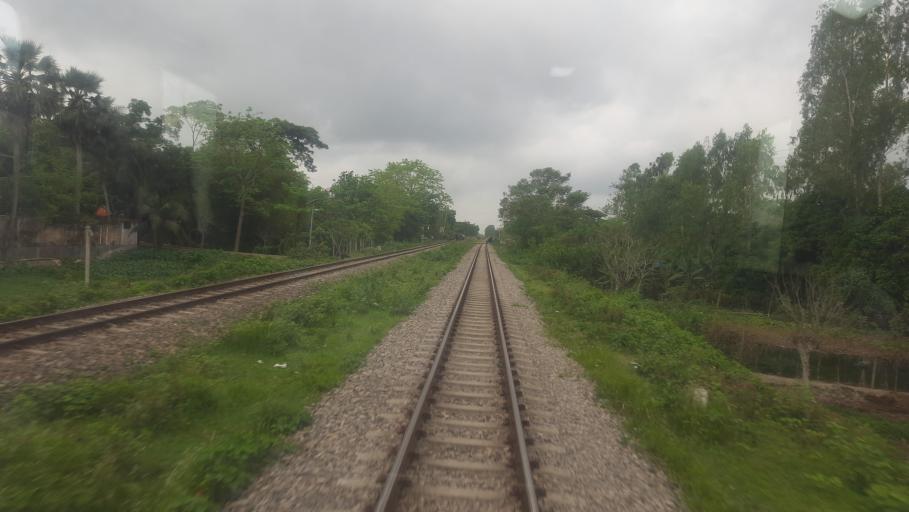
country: BD
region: Dhaka
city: Bhairab Bazar
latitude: 23.9976
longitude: 90.8799
